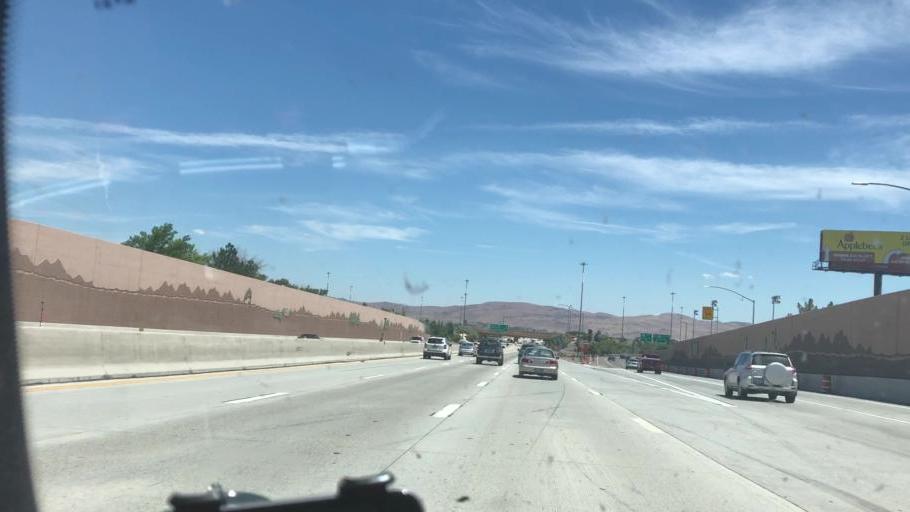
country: US
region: Nevada
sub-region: Washoe County
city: Reno
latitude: 39.5365
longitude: -119.7952
